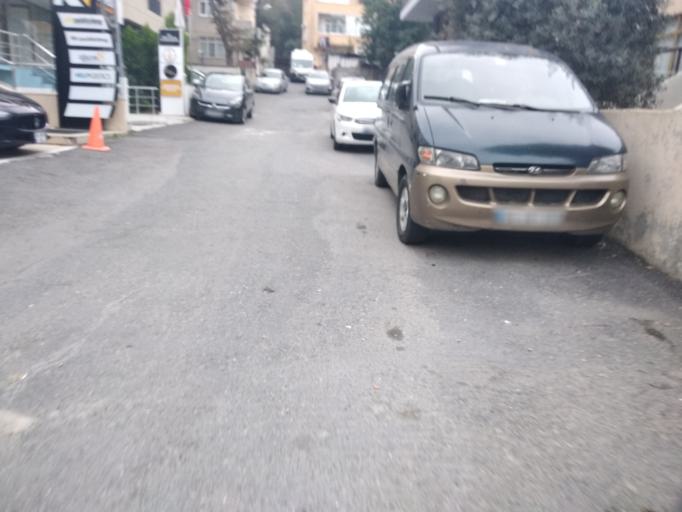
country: TR
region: Istanbul
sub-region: Atasehir
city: Atasehir
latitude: 40.9839
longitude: 29.1178
